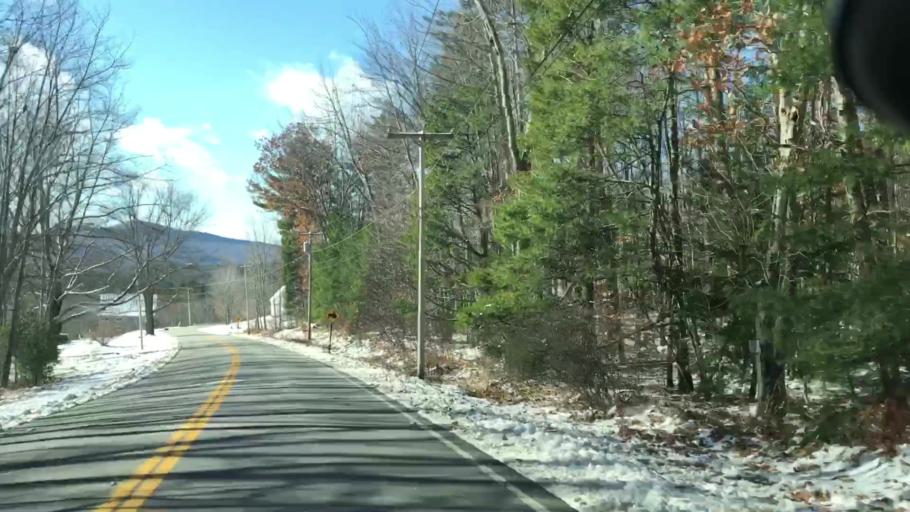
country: US
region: Maine
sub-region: Oxford County
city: Denmark
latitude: 43.9632
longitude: -70.8447
